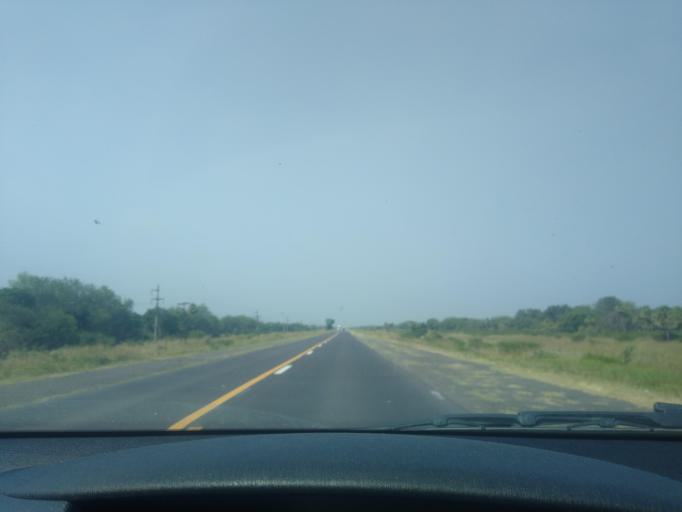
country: AR
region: Chaco
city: Fontana
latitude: -27.5414
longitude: -59.1301
